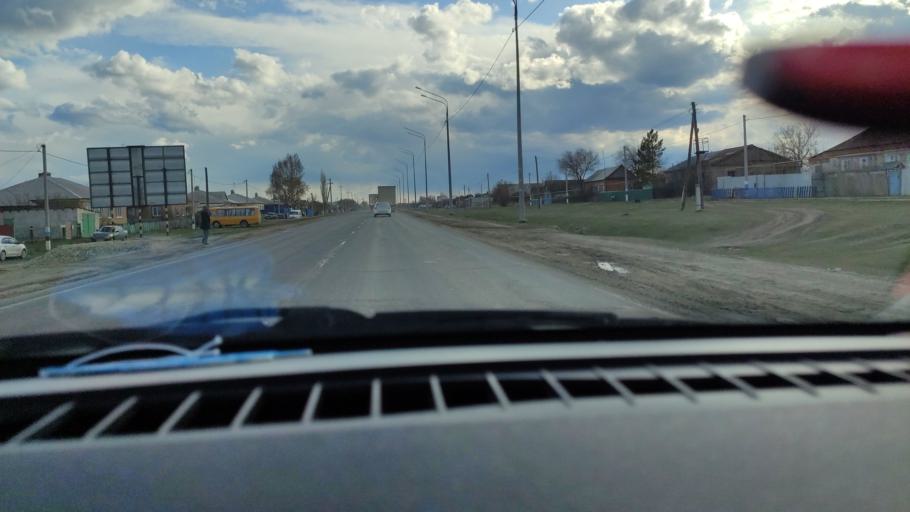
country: RU
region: Saratov
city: Sinodskoye
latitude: 51.9923
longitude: 46.6699
